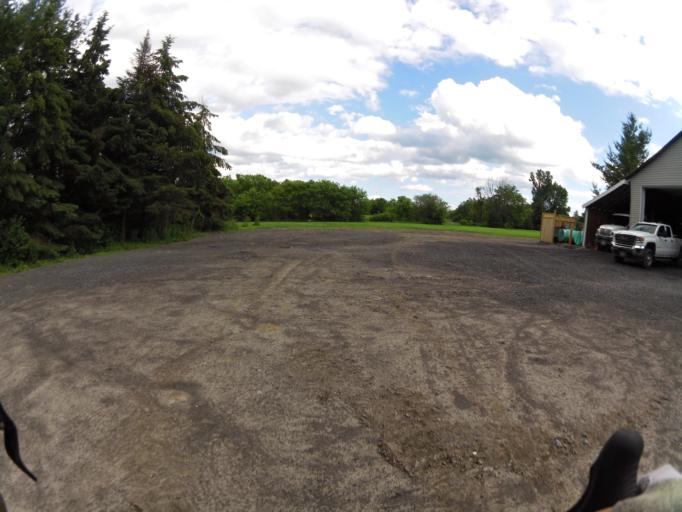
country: CA
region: Ontario
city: Bells Corners
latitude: 45.1843
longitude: -75.8339
